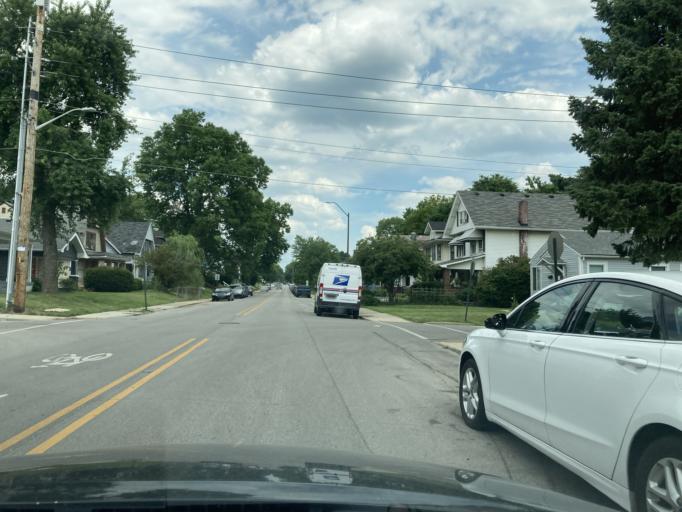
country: US
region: Indiana
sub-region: Marion County
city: Broad Ripple
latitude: 39.8262
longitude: -86.1616
